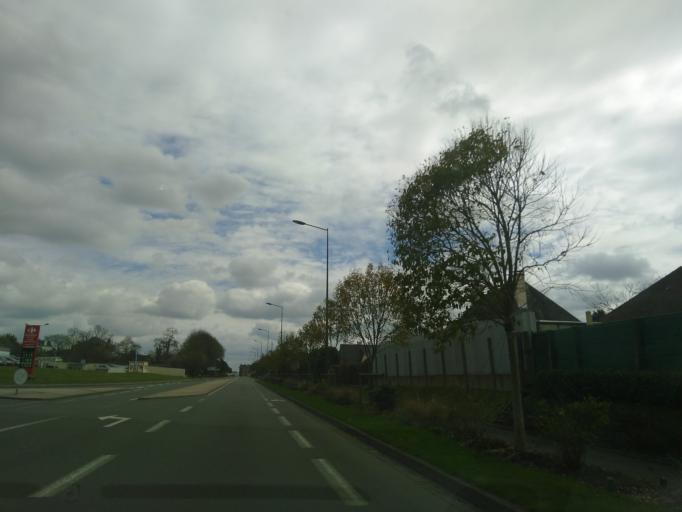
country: FR
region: Pays de la Loire
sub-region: Departement de la Mayenne
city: Mayenne
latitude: 48.3082
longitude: -0.6305
